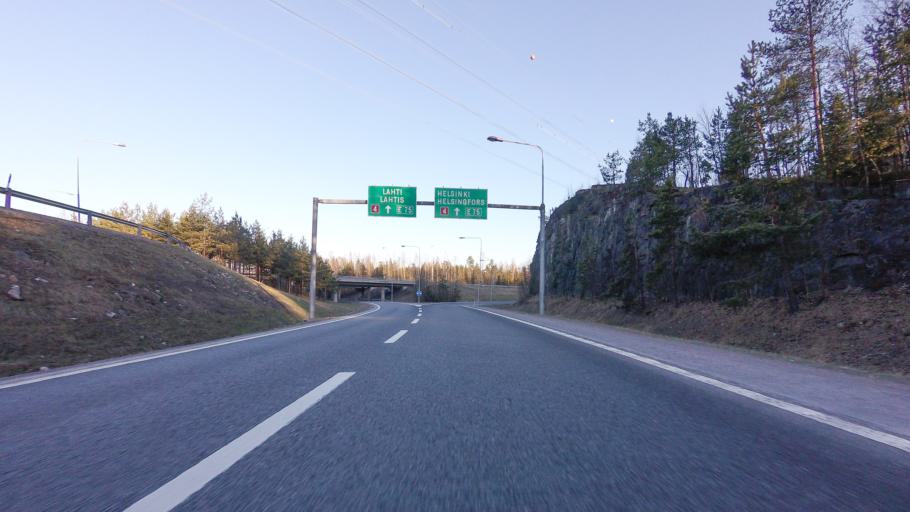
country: FI
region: Uusimaa
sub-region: Helsinki
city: Vantaa
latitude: 60.2737
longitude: 25.0848
